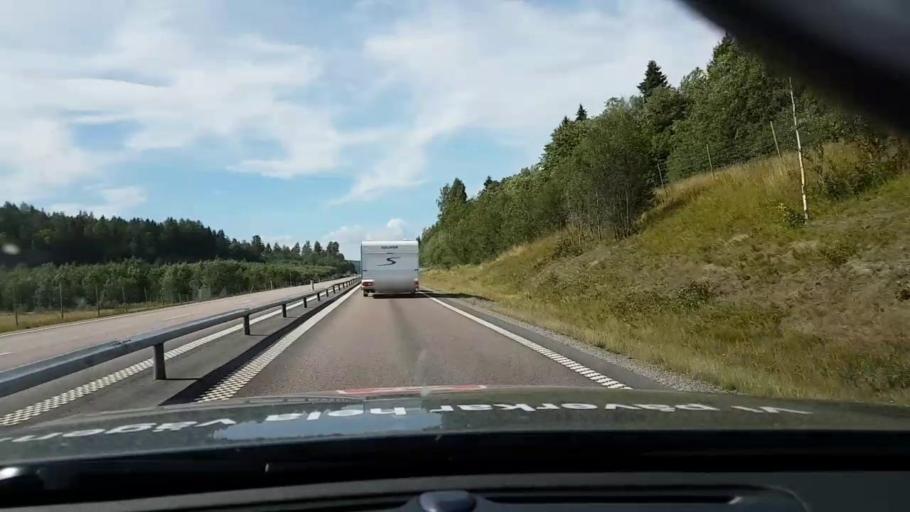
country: SE
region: Vaesternorrland
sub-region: OErnskoeldsviks Kommun
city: Ornskoldsvik
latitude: 63.3120
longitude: 18.8244
